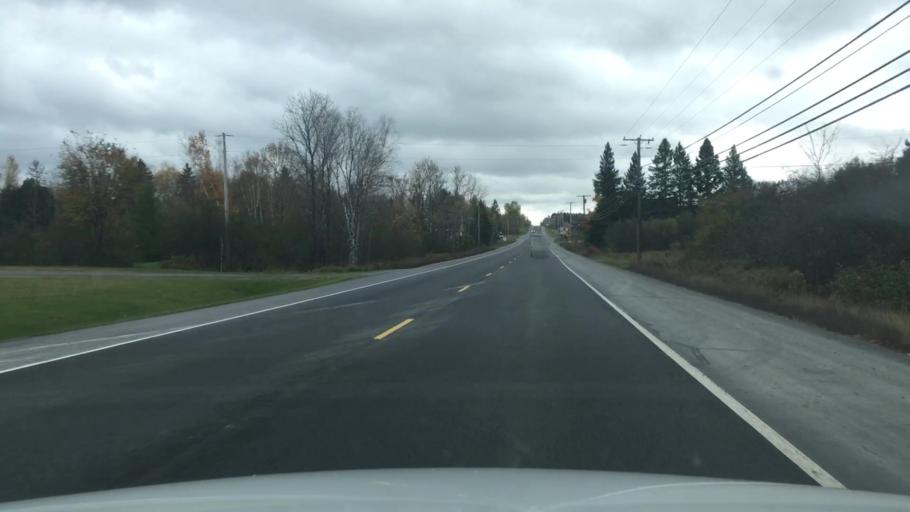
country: US
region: Maine
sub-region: Aroostook County
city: Houlton
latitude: 46.2454
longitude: -67.8408
